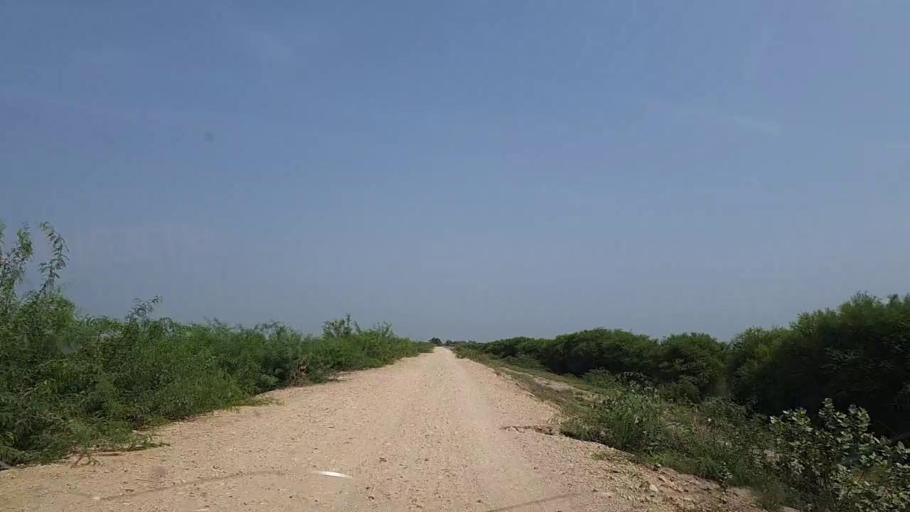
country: PK
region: Sindh
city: Ghotki
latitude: 28.0953
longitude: 69.4054
